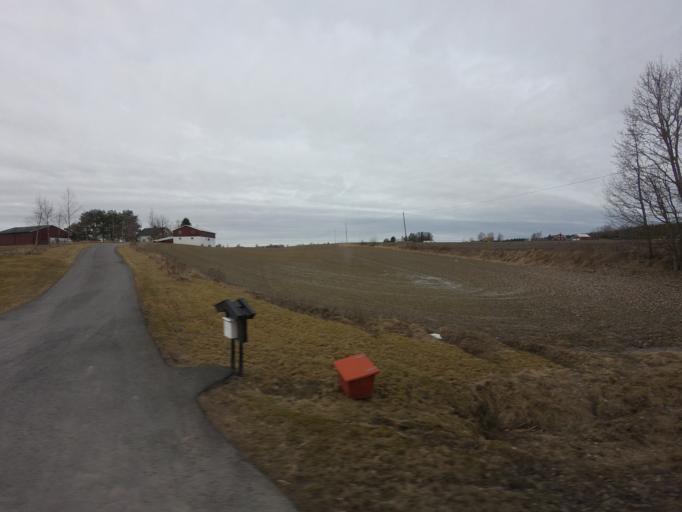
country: NO
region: Ostfold
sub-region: Trogstad
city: Skjonhaug
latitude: 59.6605
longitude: 11.3176
